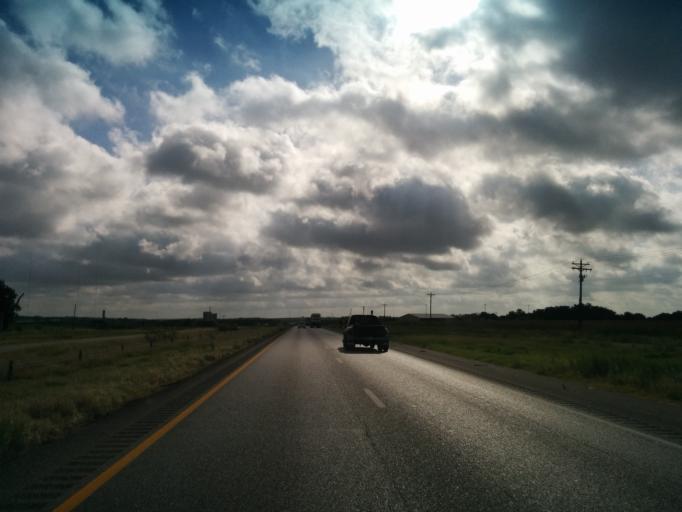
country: US
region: Texas
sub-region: Guadalupe County
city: Marion
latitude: 29.5225
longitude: -98.1294
